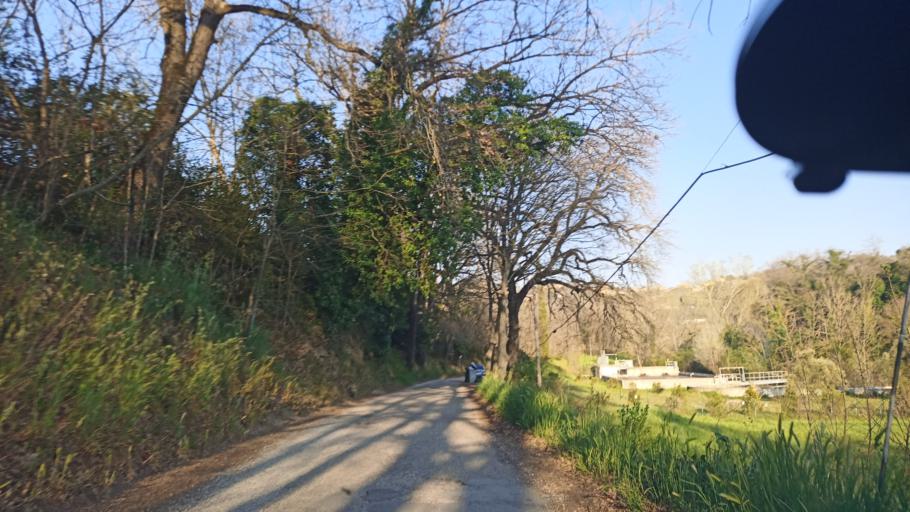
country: IT
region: Latium
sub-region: Provincia di Rieti
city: Poggio Mirteto
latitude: 42.2623
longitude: 12.6683
